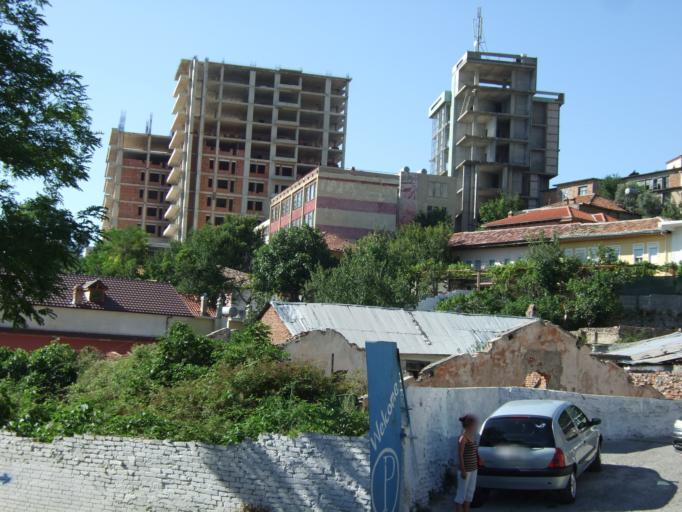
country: AL
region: Durres
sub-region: Rrethi i Krujes
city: Kruje
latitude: 41.5089
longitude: 19.7959
